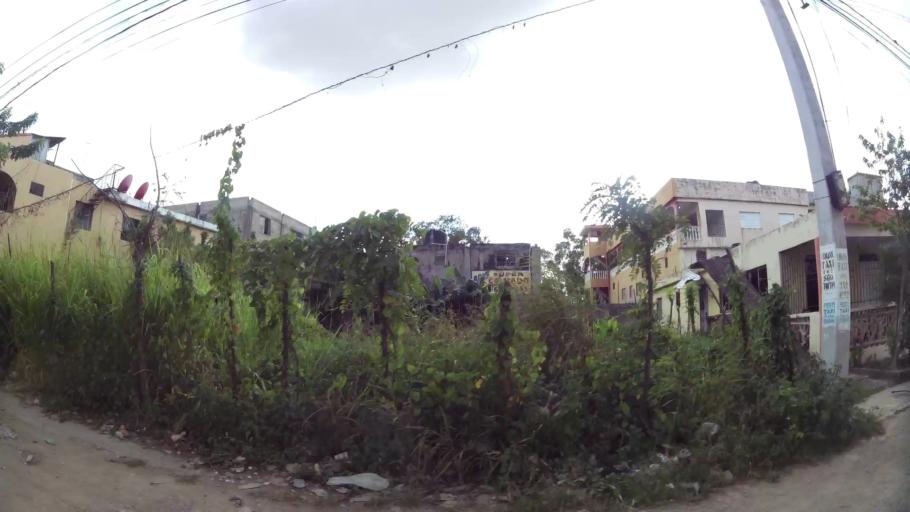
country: DO
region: Nacional
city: Ensanche Luperon
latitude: 18.5586
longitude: -69.9045
